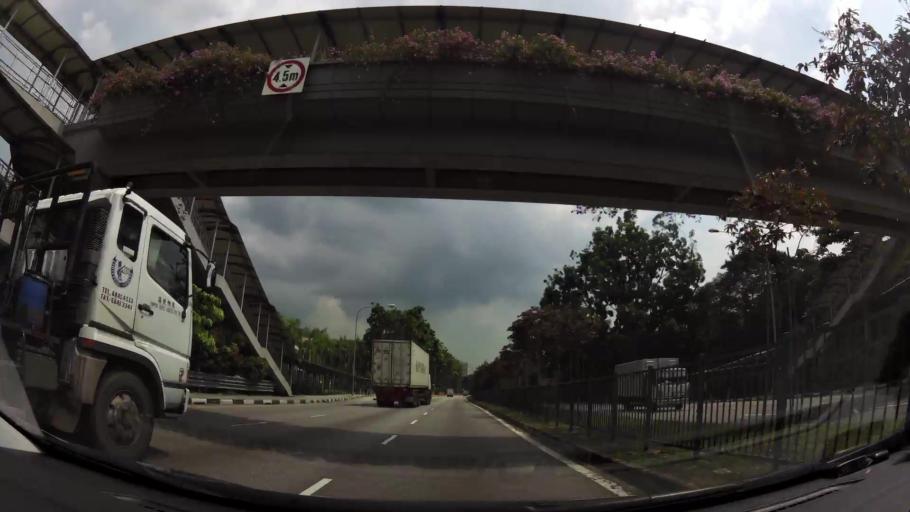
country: SG
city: Singapore
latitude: 1.2894
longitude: 103.7734
